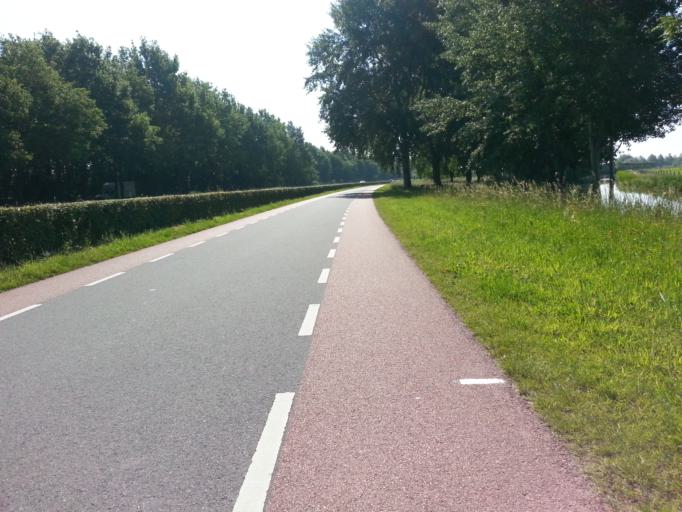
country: NL
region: Utrecht
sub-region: Gemeente Utrechtse Heuvelrug
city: Driebergen-Rijsenburg
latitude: 52.0085
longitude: 5.2848
